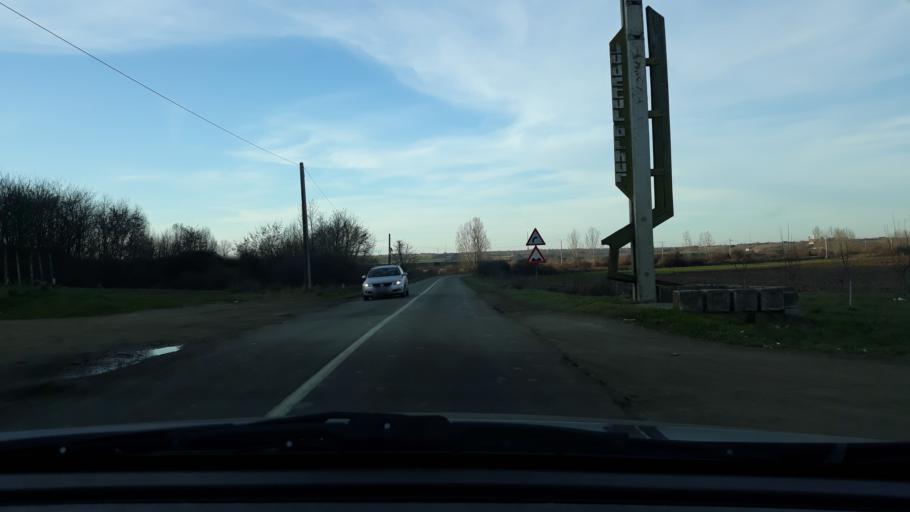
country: RO
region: Bihor
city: Foglas
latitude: 47.2328
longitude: 22.5392
